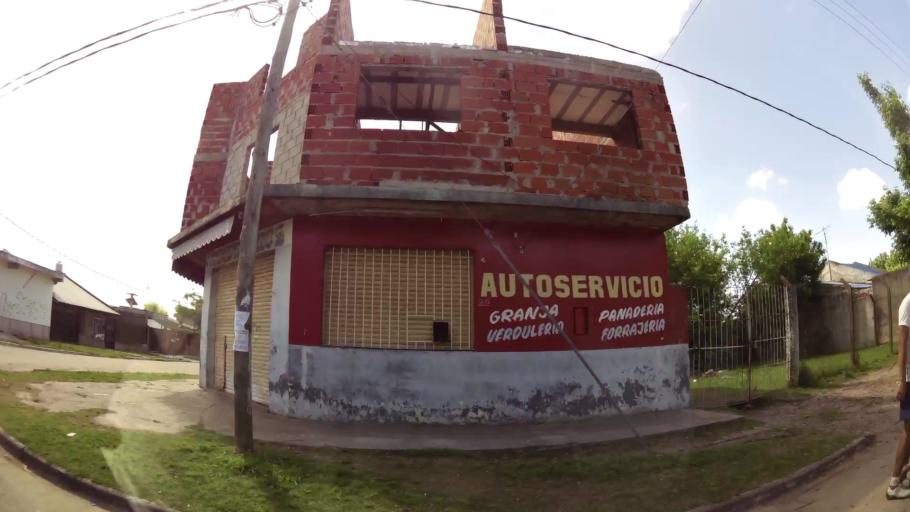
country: AR
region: Buenos Aires
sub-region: Partido de Quilmes
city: Quilmes
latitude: -34.8235
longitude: -58.2611
